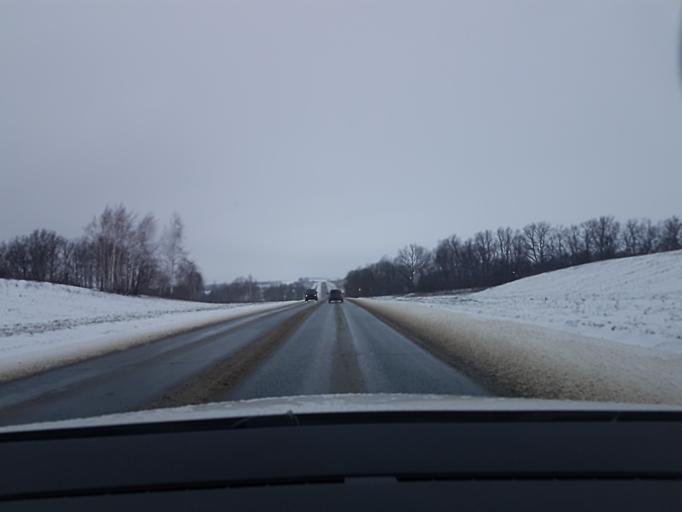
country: RU
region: Moskovskaya
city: Serebryanyye Prudy
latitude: 54.4100
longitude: 38.6629
